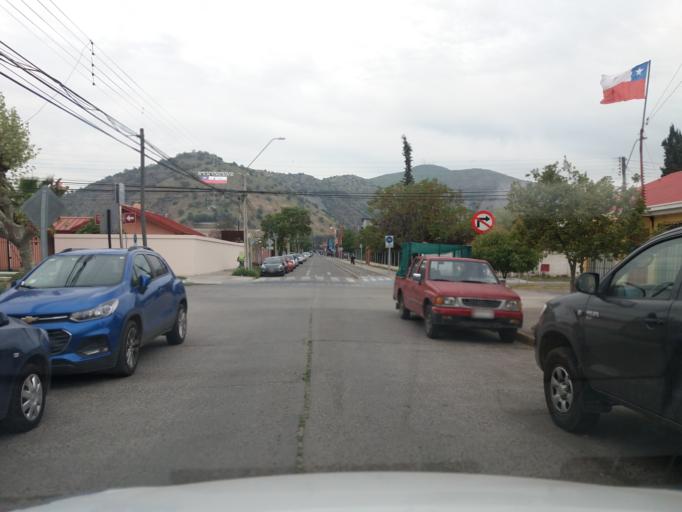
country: CL
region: Valparaiso
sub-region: Provincia de Quillota
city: Hacienda La Calera
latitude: -32.7839
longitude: -71.1916
